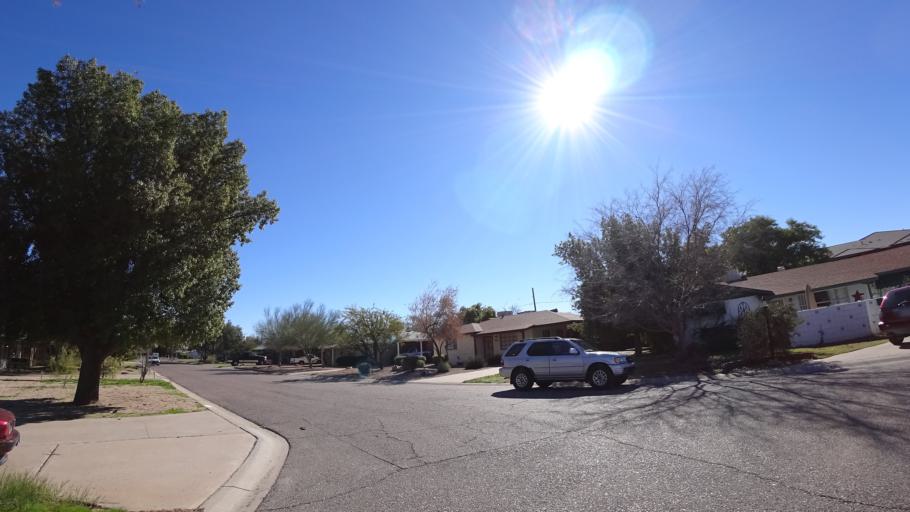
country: US
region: Arizona
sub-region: Maricopa County
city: Phoenix
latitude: 33.5187
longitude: -112.0622
